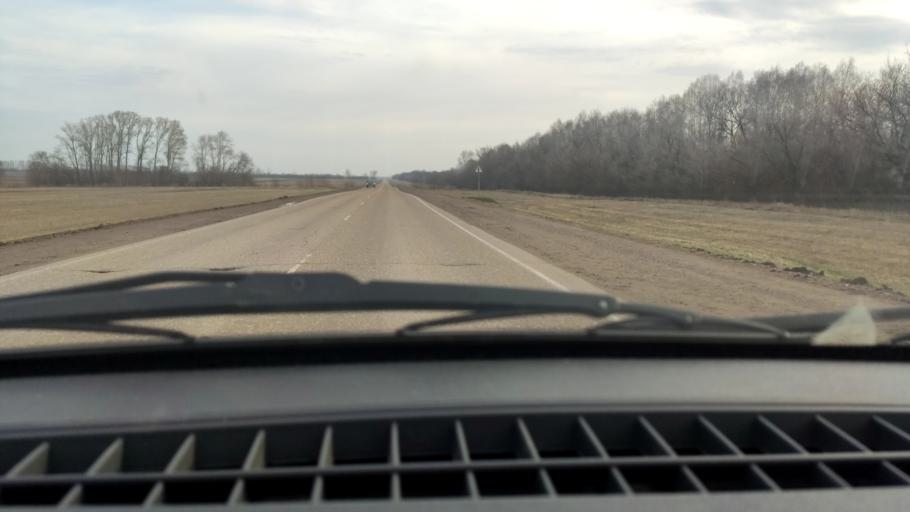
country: RU
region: Bashkortostan
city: Davlekanovo
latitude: 54.2558
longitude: 55.0855
